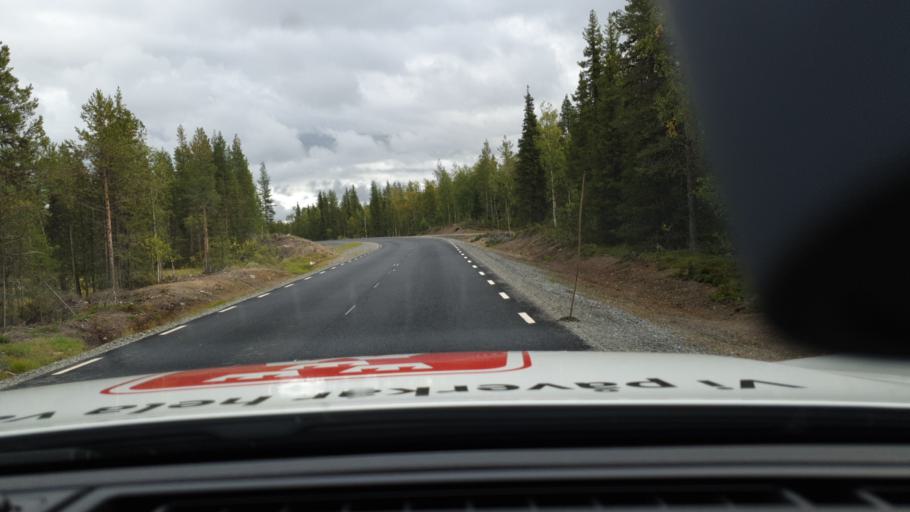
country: SE
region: Norrbotten
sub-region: Gallivare Kommun
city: Gaellivare
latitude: 66.8677
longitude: 21.2022
